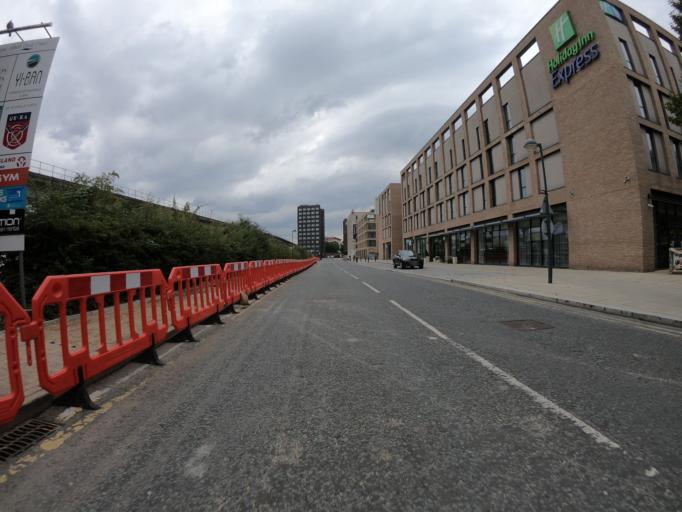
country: GB
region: England
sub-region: Greater London
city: East Ham
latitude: 51.5082
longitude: 0.0437
